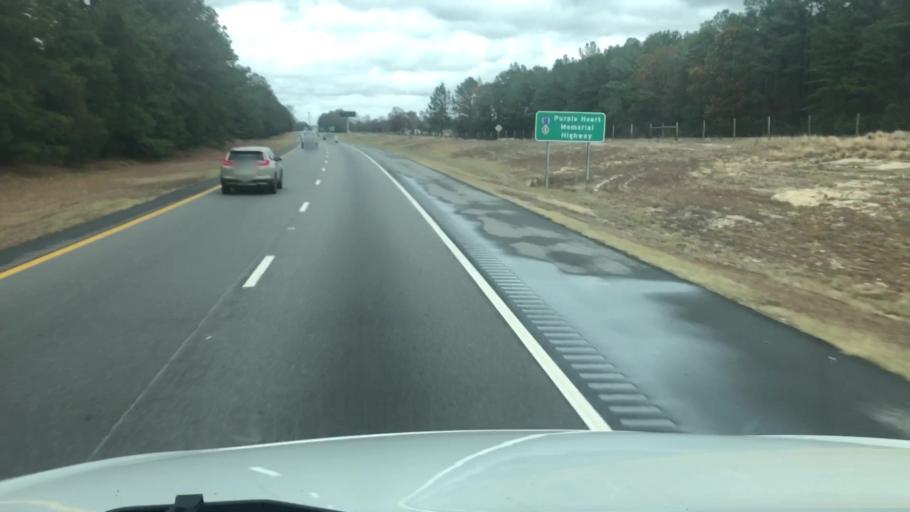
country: US
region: North Carolina
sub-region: Cumberland County
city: Vander
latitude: 35.0604
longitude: -78.7945
